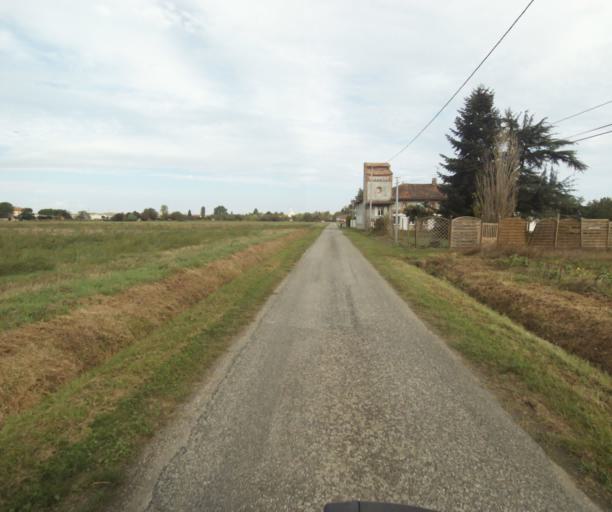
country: FR
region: Midi-Pyrenees
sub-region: Departement du Tarn-et-Garonne
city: Montech
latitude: 43.9409
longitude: 1.2218
